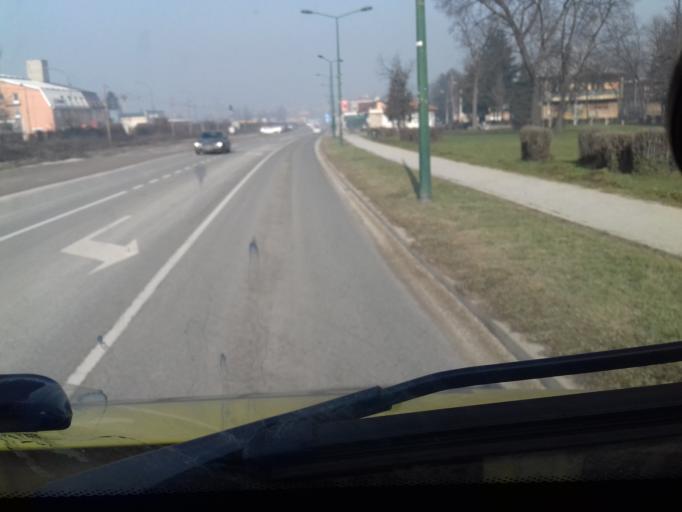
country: BA
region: Federation of Bosnia and Herzegovina
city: Ilijas
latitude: 43.9562
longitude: 18.2644
